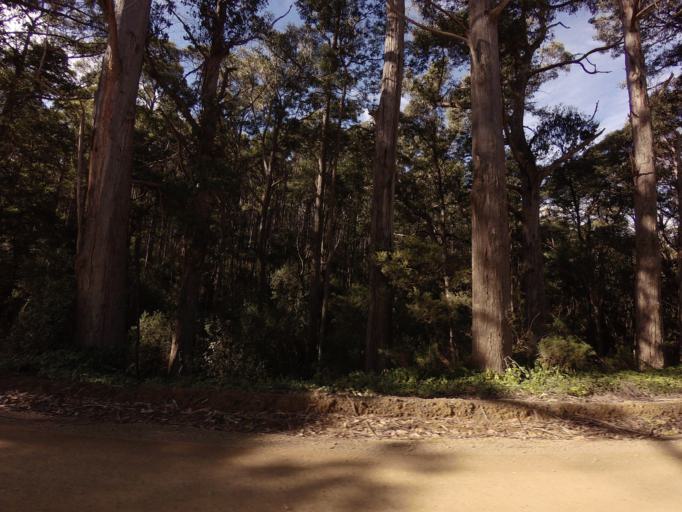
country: AU
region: Tasmania
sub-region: Clarence
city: Sandford
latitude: -43.1327
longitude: 147.7664
